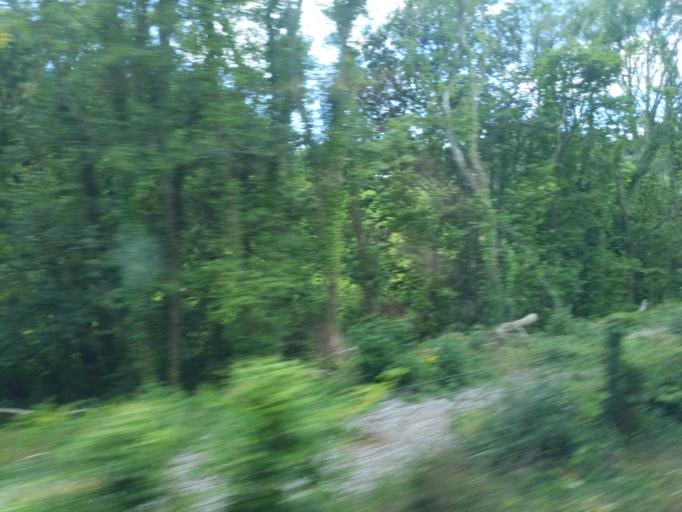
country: GB
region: England
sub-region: Cornwall
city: Saltash
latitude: 50.3943
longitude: -4.2557
